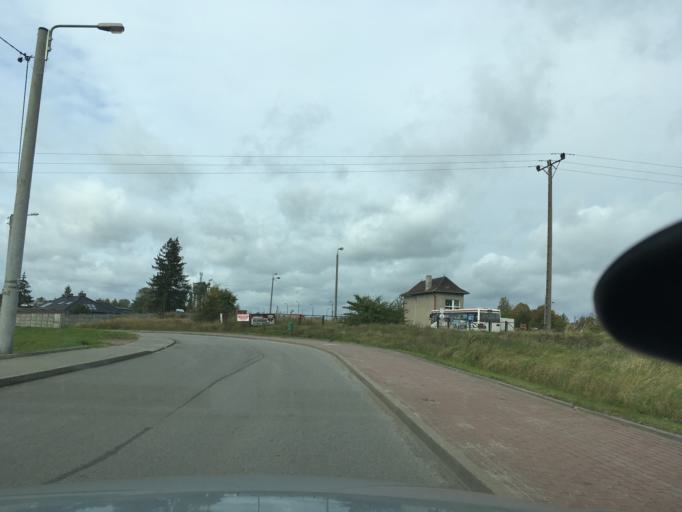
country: PL
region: Pomeranian Voivodeship
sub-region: Powiat koscierski
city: Koscierzyna
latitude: 54.1153
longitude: 18.0033
